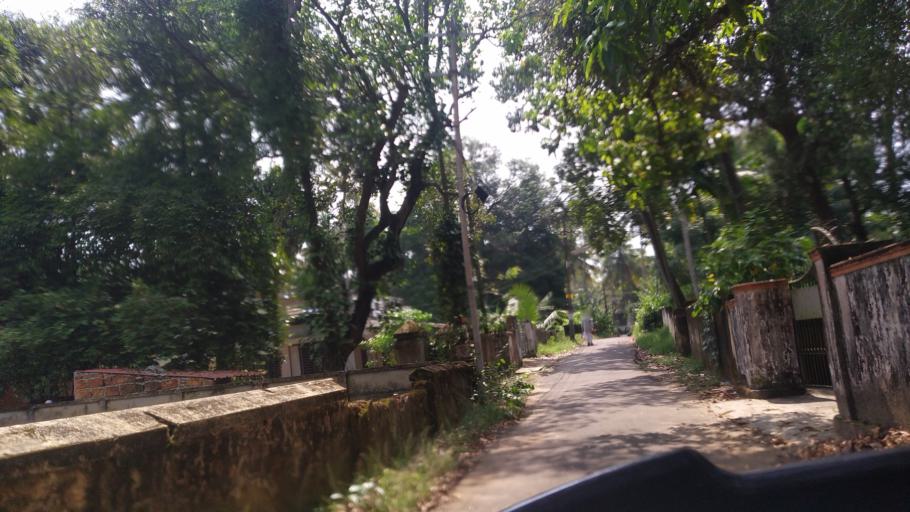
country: IN
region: Kerala
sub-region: Ernakulam
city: Elur
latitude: 10.0557
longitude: 76.2181
